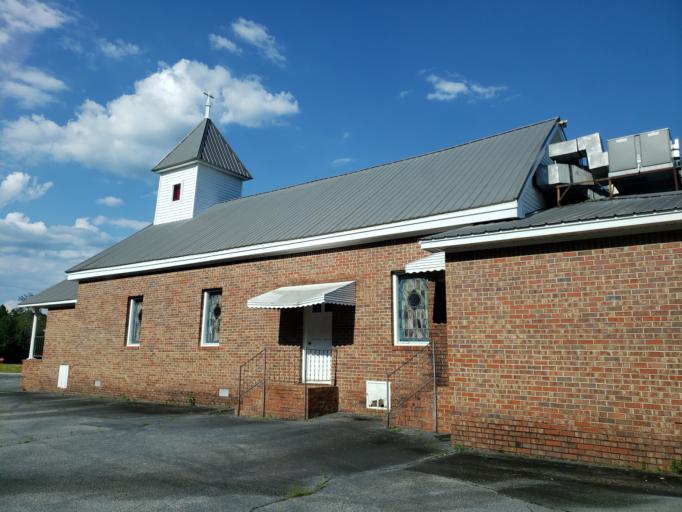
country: US
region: Georgia
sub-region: Haralson County
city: Bremen
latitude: 33.7823
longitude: -85.1111
